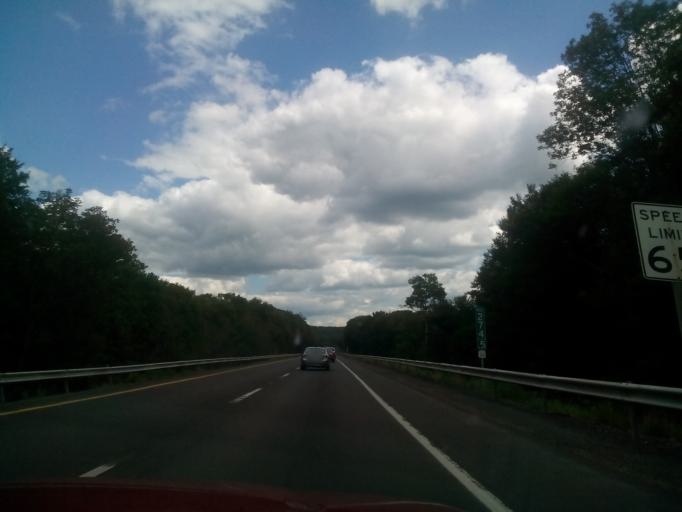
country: US
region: Pennsylvania
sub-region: Luzerne County
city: White Haven
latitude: 41.0594
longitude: -75.7401
